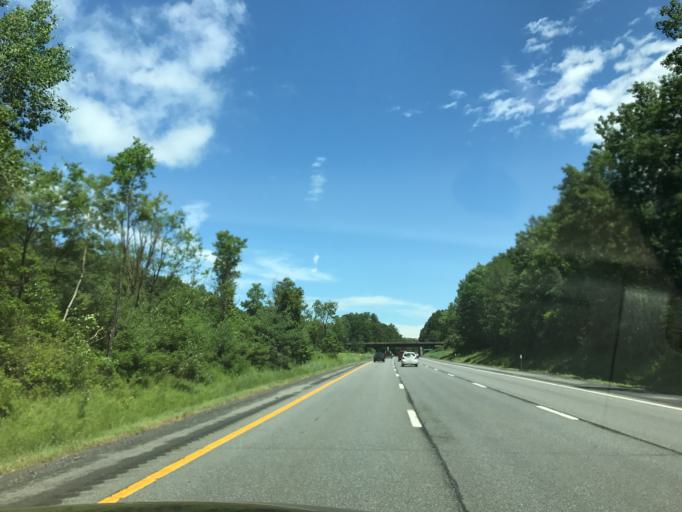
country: US
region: New York
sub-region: Warren County
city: West Glens Falls
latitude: 43.1882
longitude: -73.7050
